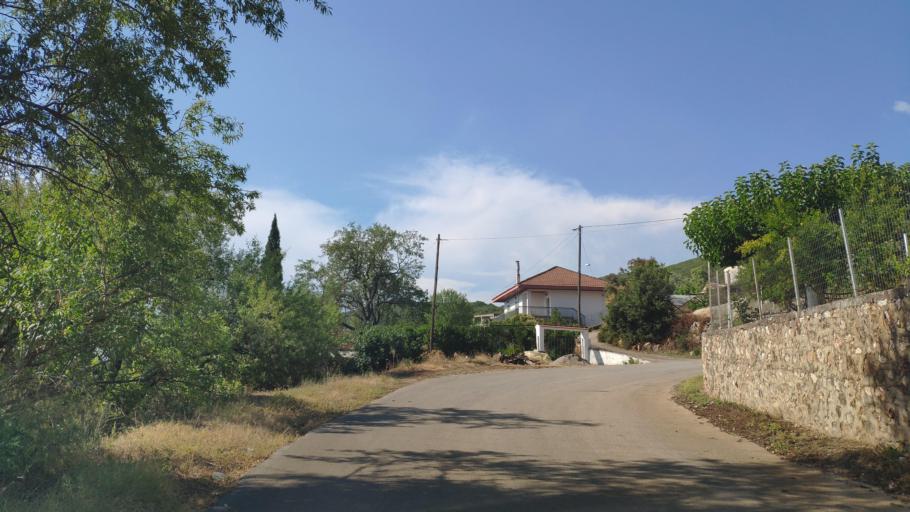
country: GR
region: West Greece
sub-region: Nomos Aitolias kai Akarnanias
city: Fitiai
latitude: 38.6571
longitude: 21.1475
